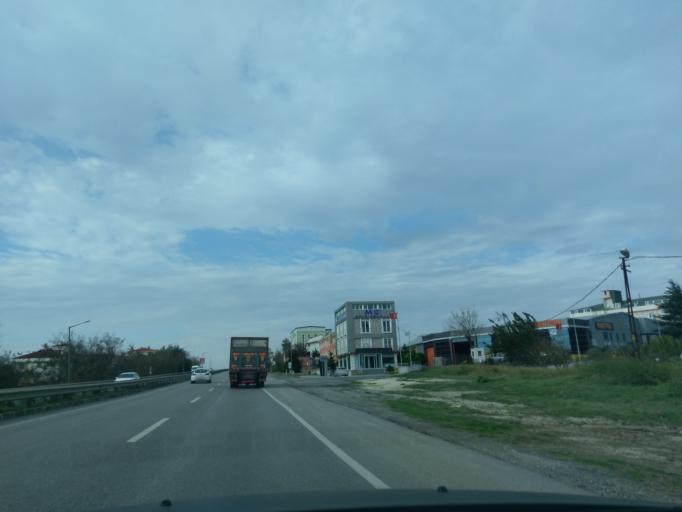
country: TR
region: Istanbul
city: Celaliye
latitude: 41.0487
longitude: 28.3968
